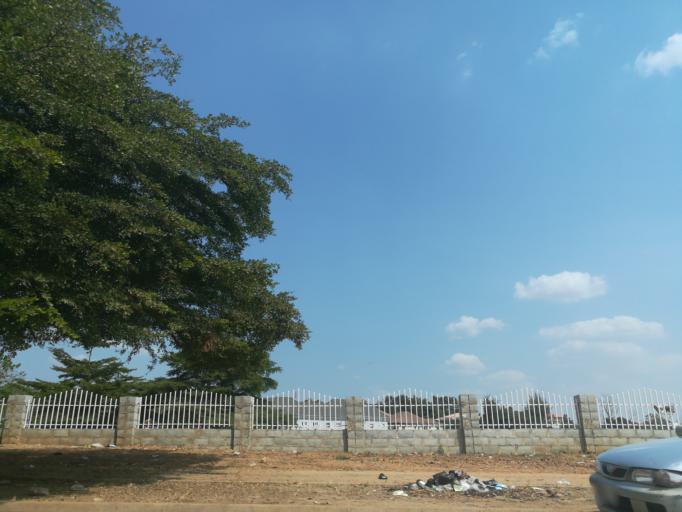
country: NG
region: Abuja Federal Capital Territory
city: Abuja
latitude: 9.0631
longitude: 7.4361
